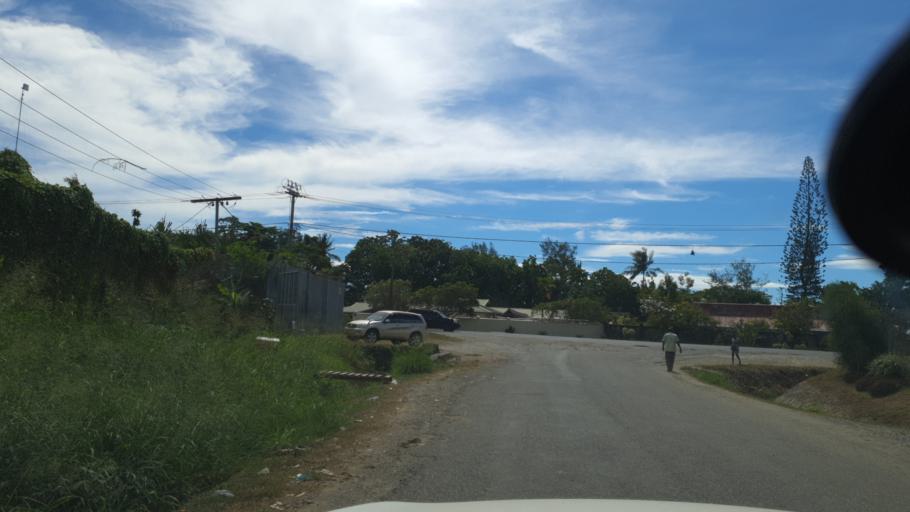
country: SB
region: Guadalcanal
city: Honiara
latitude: -9.4264
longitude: 159.9318
